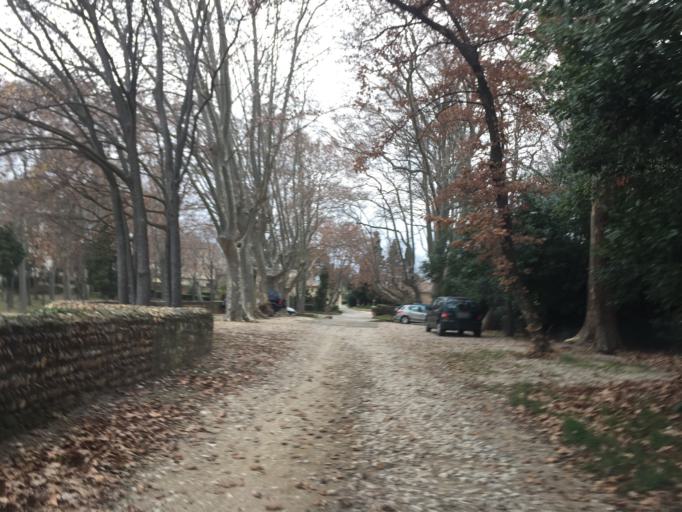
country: FR
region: Provence-Alpes-Cote d'Azur
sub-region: Departement du Vaucluse
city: Chateauneuf-du-Pape
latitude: 44.0483
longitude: 4.8590
